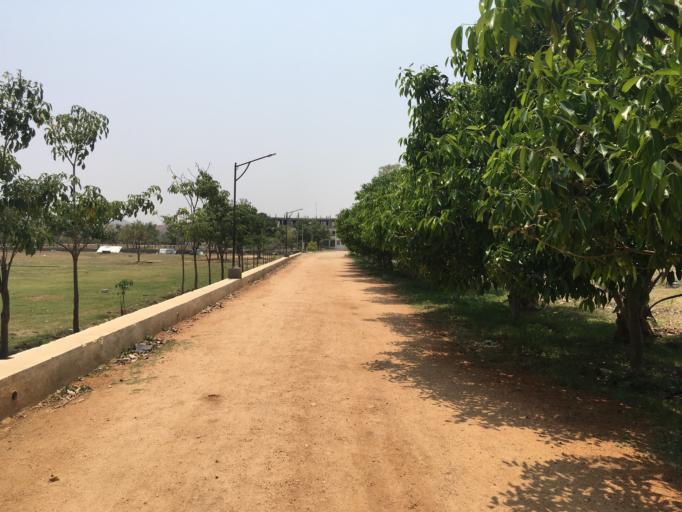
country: IN
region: Andhra Pradesh
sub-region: Anantapur
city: Puttaparthi
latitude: 14.1362
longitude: 77.7788
